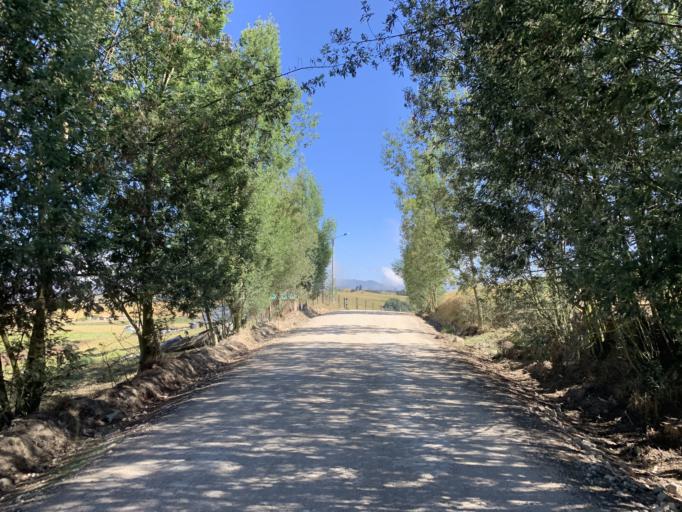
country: CO
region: Boyaca
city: Tuta
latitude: 5.6622
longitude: -73.1514
